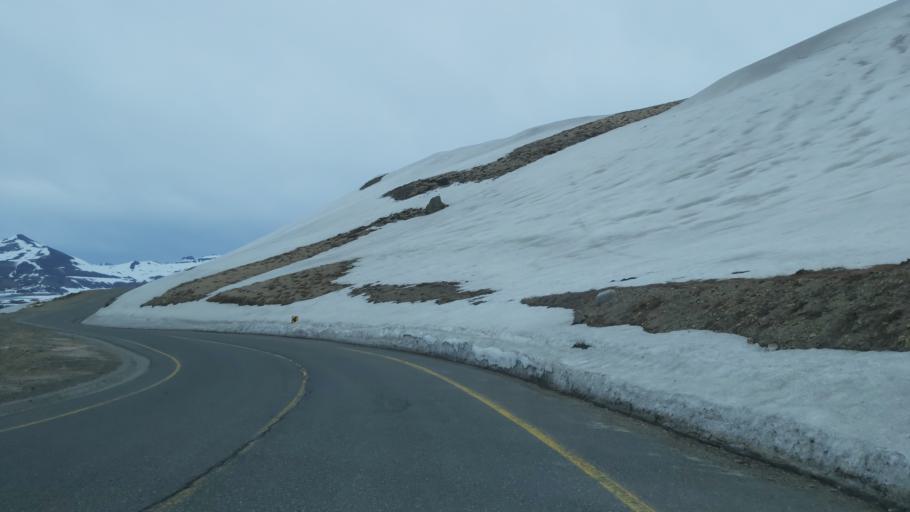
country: CL
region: Maule
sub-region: Provincia de Linares
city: Colbun
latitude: -36.0205
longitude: -70.5000
